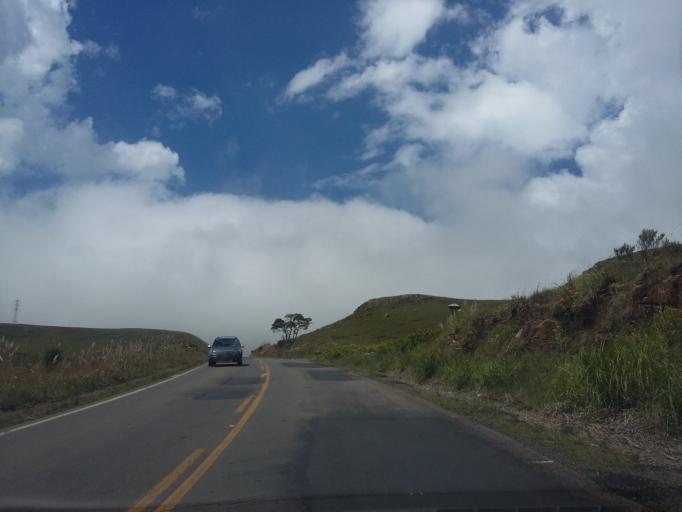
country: BR
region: Santa Catarina
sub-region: Lauro Muller
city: Lauro Muller
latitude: -28.3718
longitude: -49.5677
